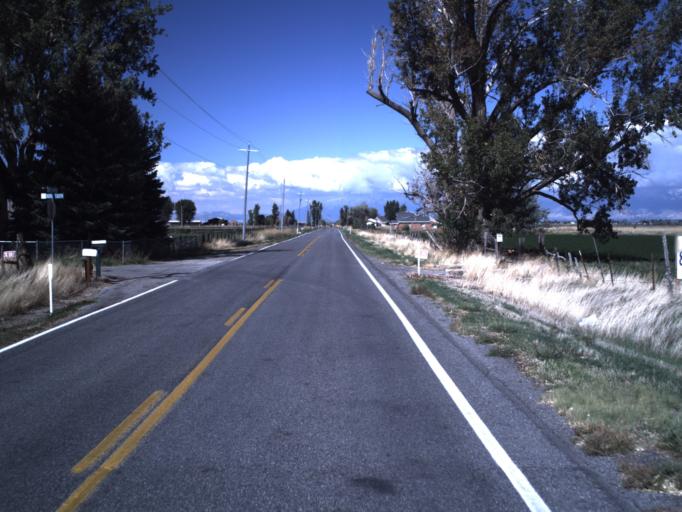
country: US
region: Utah
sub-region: Utah County
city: West Mountain
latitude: 40.0848
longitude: -111.7879
